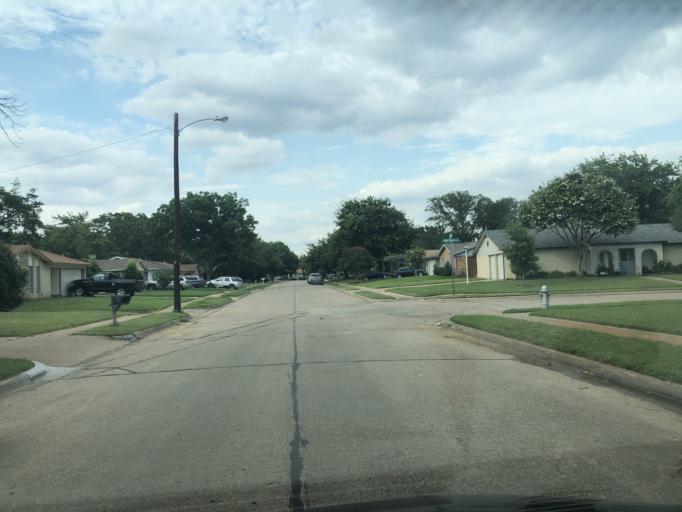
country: US
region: Texas
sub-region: Dallas County
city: Irving
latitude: 32.7937
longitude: -96.9761
